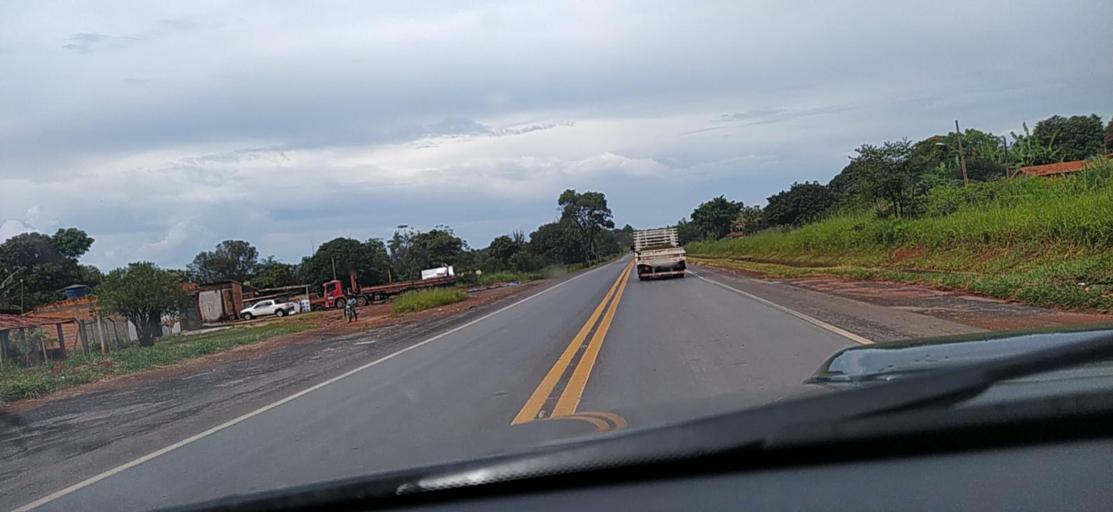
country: BR
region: Minas Gerais
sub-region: Montes Claros
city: Montes Claros
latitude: -16.8764
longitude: -43.8604
